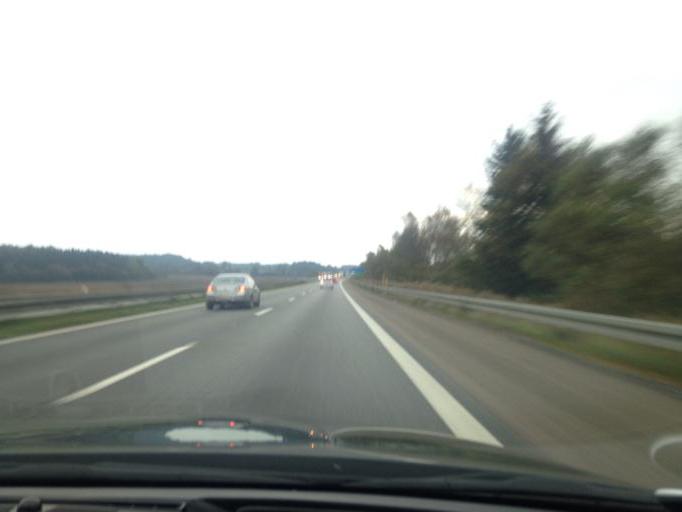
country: DK
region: South Denmark
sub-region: Kolding Kommune
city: Christiansfeld
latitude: 55.3446
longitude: 9.4447
